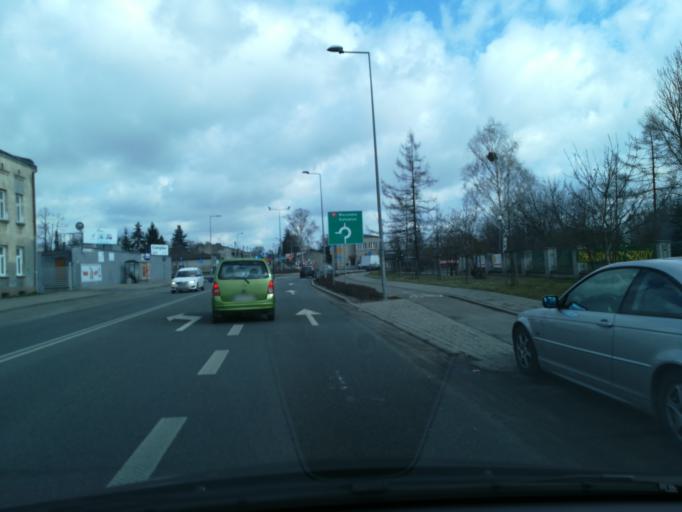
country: PL
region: Silesian Voivodeship
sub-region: Czestochowa
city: Czestochowa
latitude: 50.8230
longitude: 19.1334
